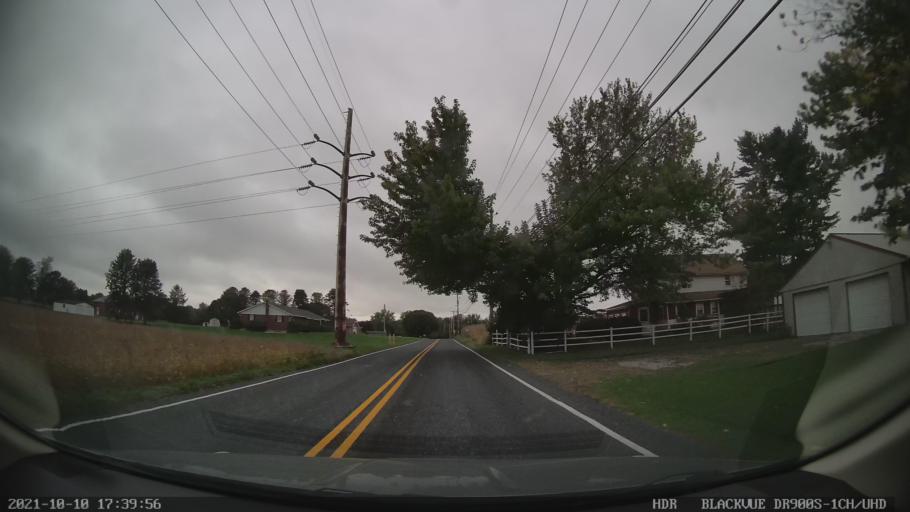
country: US
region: Pennsylvania
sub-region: Berks County
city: Topton
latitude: 40.5137
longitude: -75.6983
